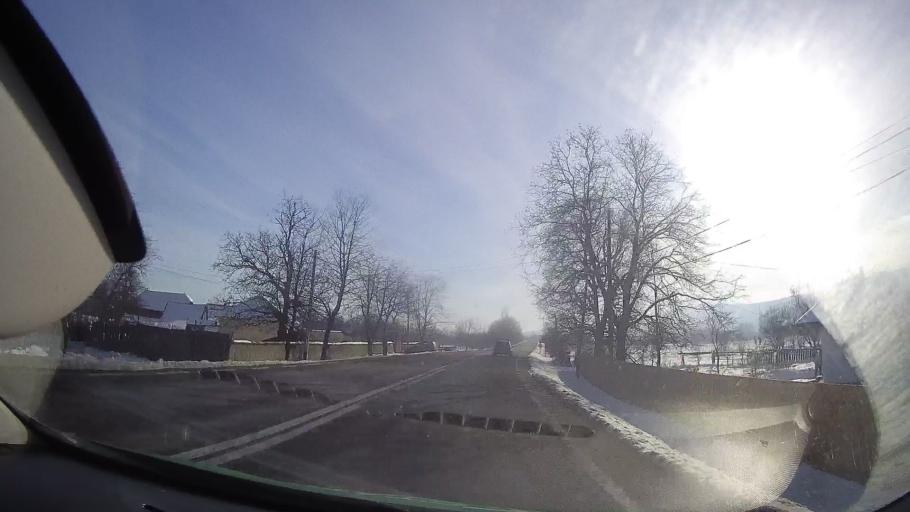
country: RO
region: Neamt
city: Bodesti
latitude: 47.0507
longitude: 26.4030
